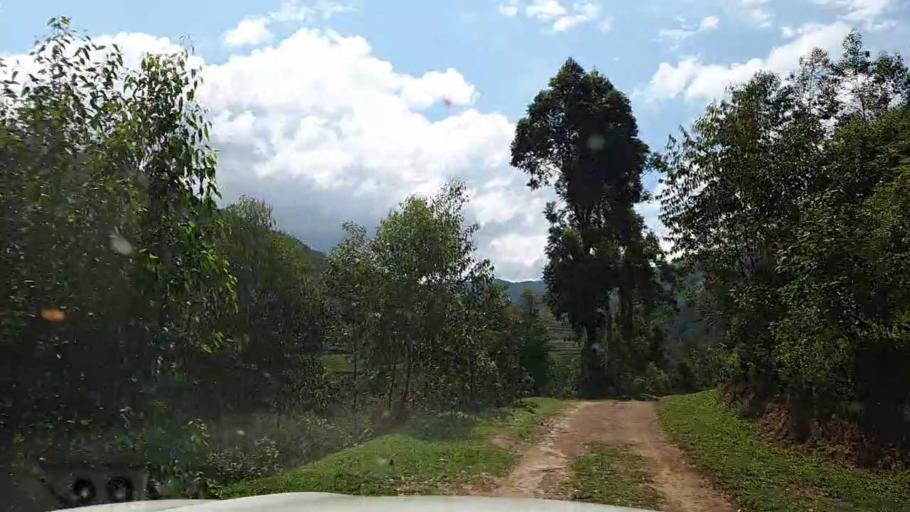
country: RW
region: Southern Province
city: Gikongoro
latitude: -2.3613
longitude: 29.5373
